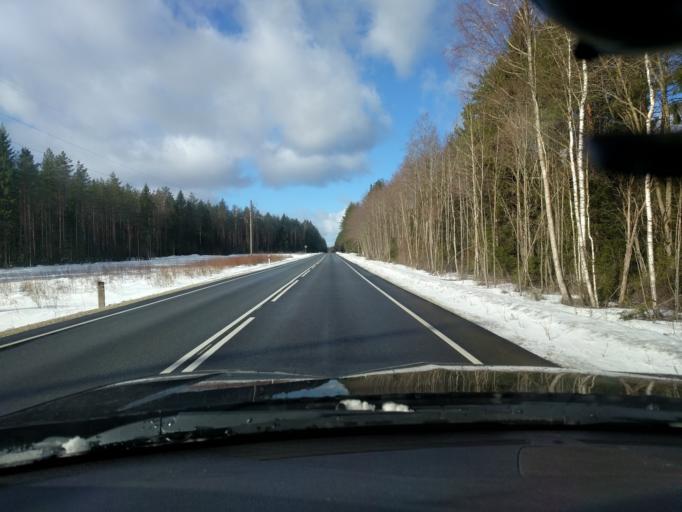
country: EE
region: Harju
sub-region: Kuusalu vald
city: Kuusalu
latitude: 59.2065
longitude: 25.5650
